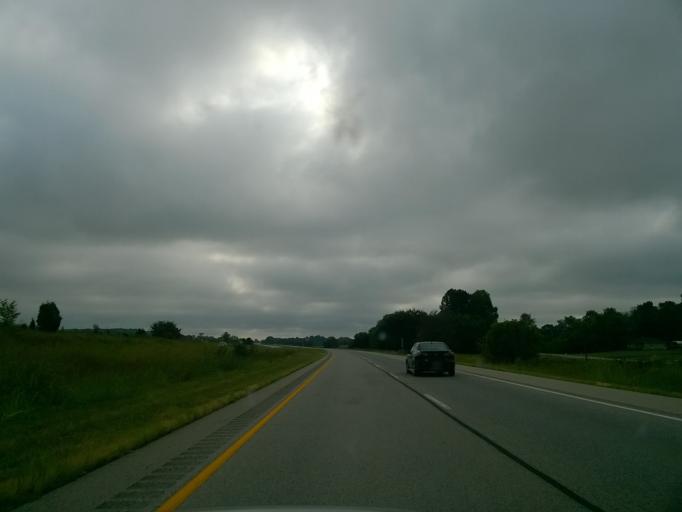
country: US
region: Indiana
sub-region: Harrison County
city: Corydon
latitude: 38.2413
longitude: -86.1923
